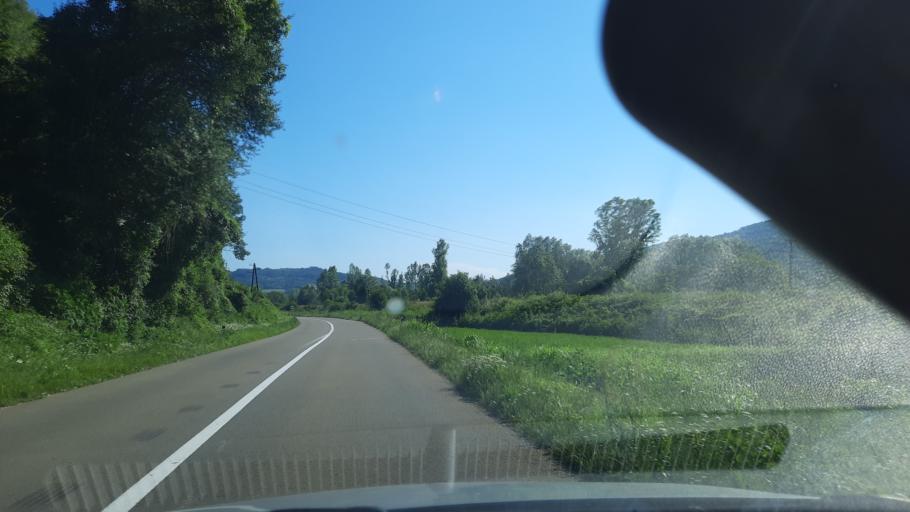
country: RS
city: Turija
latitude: 44.5083
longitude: 21.6334
